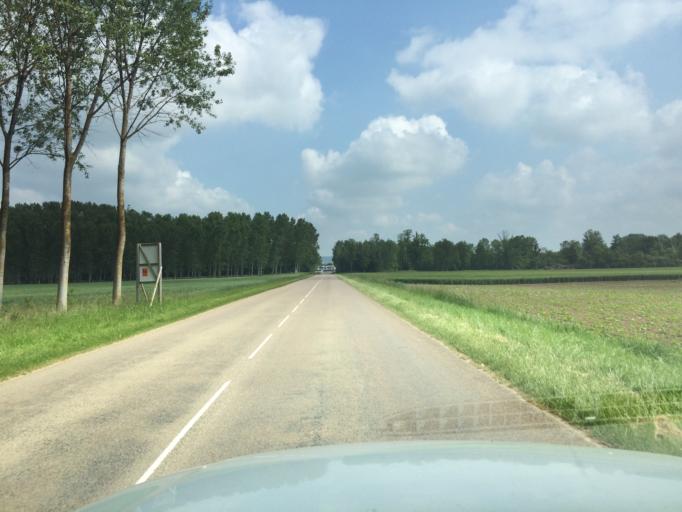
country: FR
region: Bourgogne
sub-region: Departement de l'Yonne
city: Laroche-Saint-Cydroine
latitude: 47.9524
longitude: 3.4466
